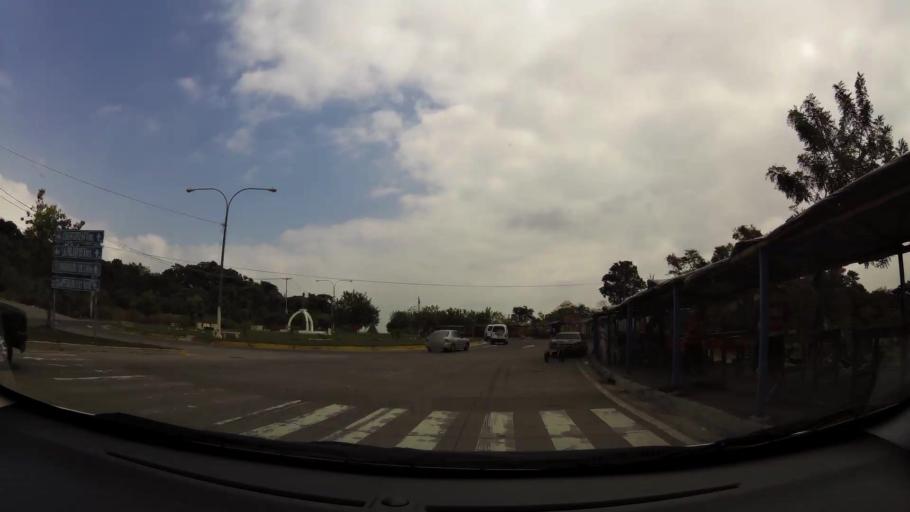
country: SV
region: San Salvador
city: Mejicanos
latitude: 13.7195
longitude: -89.2406
